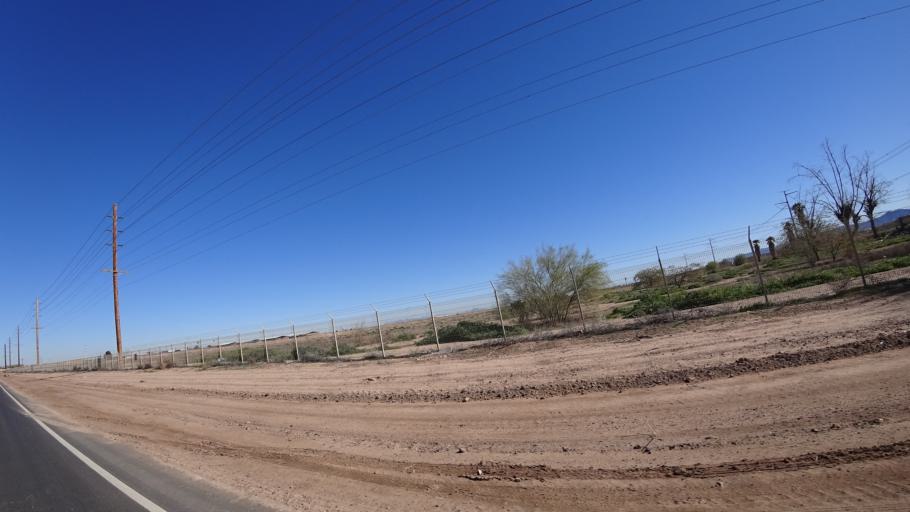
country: US
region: Arizona
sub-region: Maricopa County
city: Tolleson
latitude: 33.3994
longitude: -112.2543
